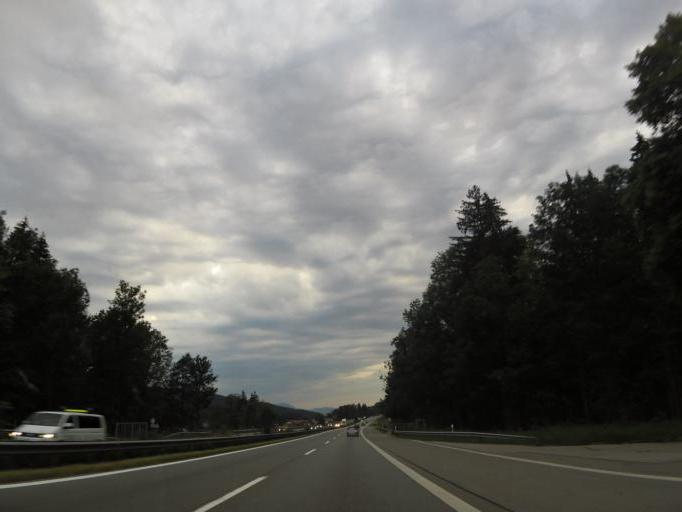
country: DE
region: Bavaria
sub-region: Upper Bavaria
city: Frasdorf
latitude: 47.7983
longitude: 12.2507
